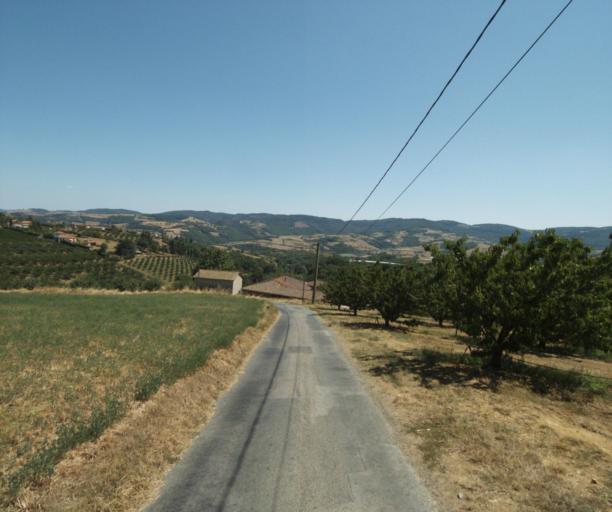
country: FR
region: Rhone-Alpes
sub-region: Departement du Rhone
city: Bessenay
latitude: 45.7751
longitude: 4.5371
